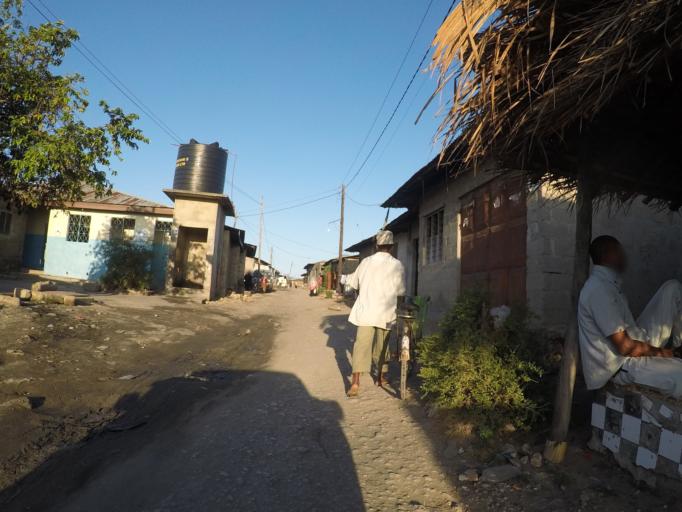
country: TZ
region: Zanzibar Urban/West
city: Zanzibar
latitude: -6.1580
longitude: 39.2137
